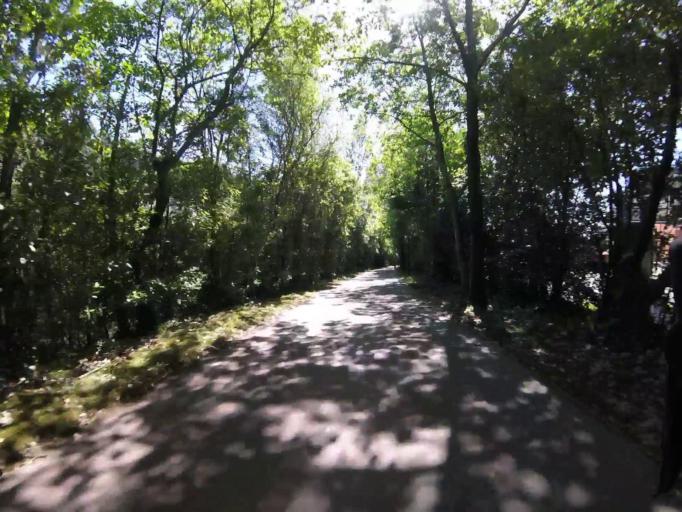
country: ES
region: Basque Country
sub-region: Provincia de Guipuzcoa
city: Irun
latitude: 43.3438
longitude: -1.7585
